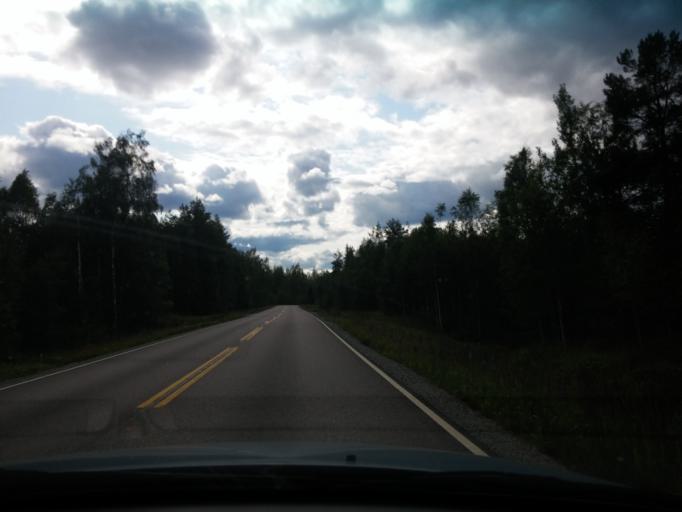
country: FI
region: Central Finland
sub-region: Saarijaervi-Viitasaari
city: Pylkoenmaeki
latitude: 62.6207
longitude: 24.7723
